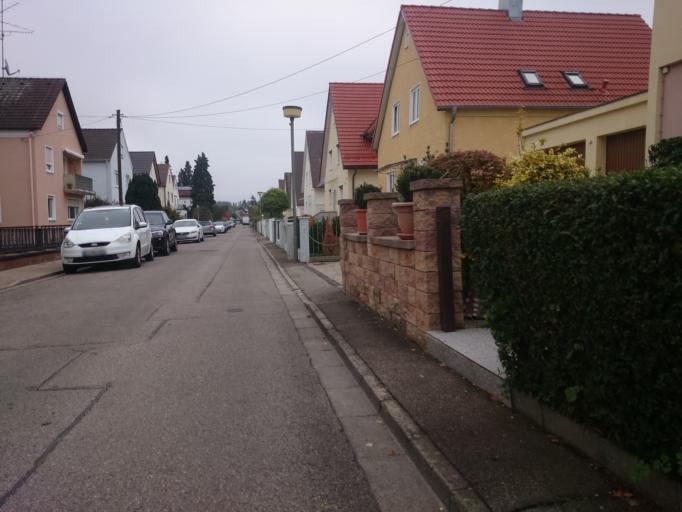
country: DE
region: Bavaria
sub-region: Swabia
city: Konigsbrunn
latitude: 48.2938
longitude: 10.8952
